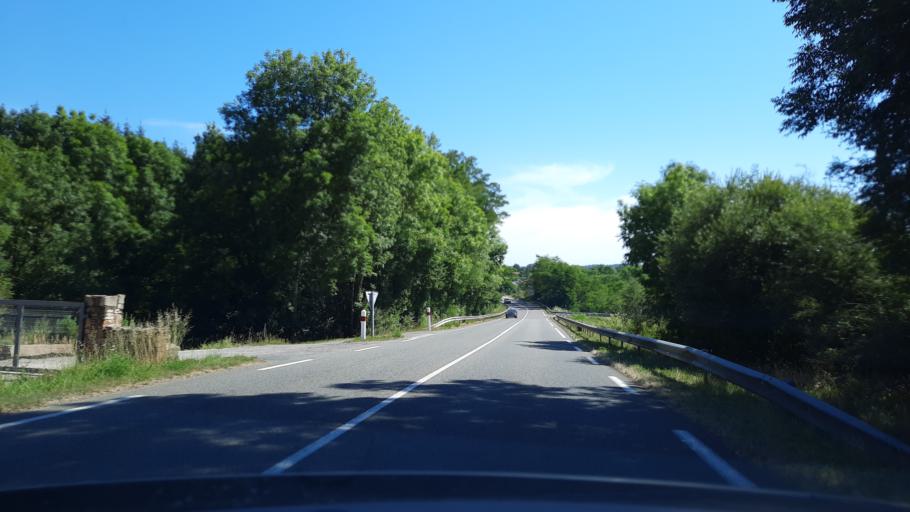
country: FR
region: Midi-Pyrenees
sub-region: Departement de l'Aveyron
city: Montbazens
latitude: 44.4556
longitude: 2.2186
